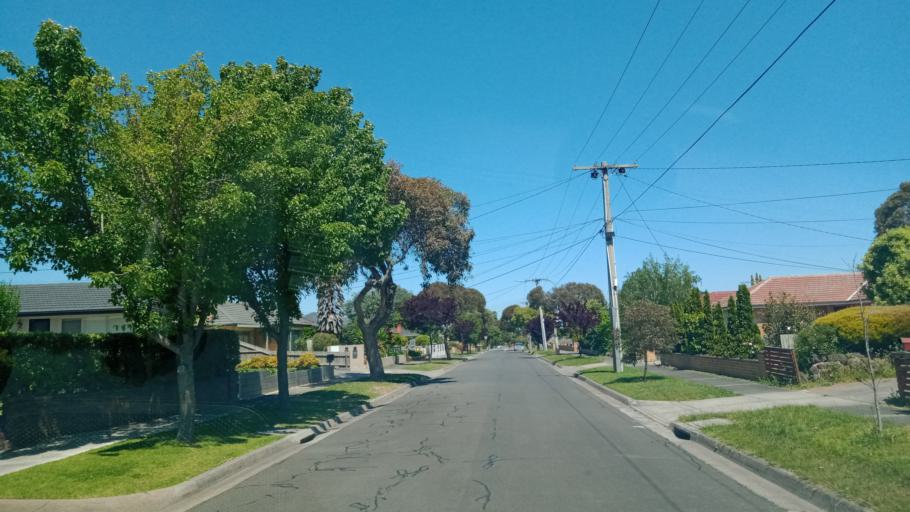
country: AU
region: Victoria
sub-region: Greater Dandenong
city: Springvale
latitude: -37.9275
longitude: 145.1647
